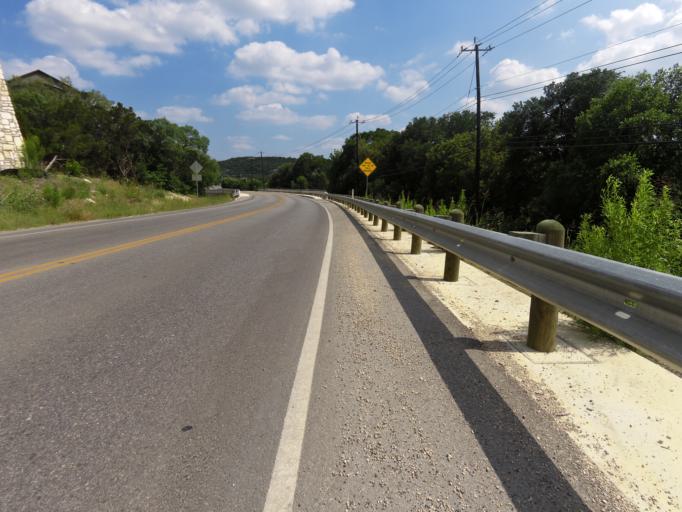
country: US
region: Texas
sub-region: Bexar County
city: Cross Mountain
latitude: 29.6178
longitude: -98.6371
